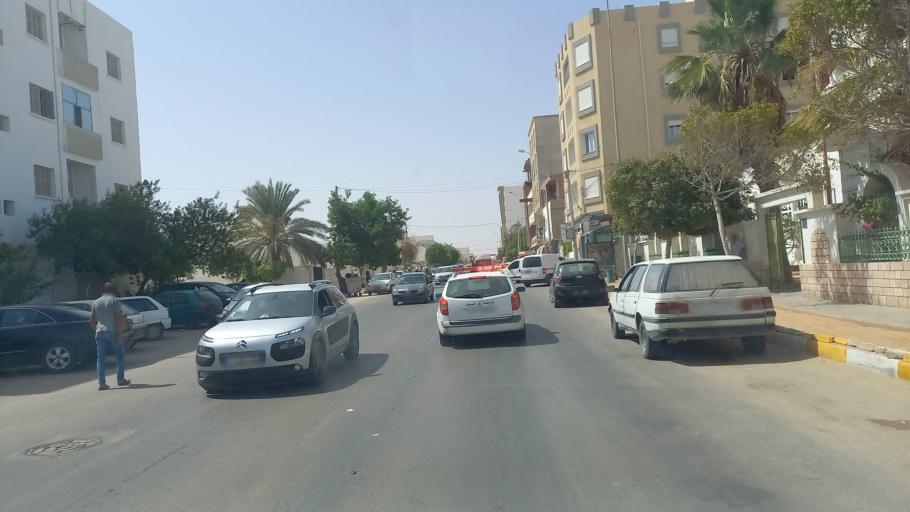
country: TN
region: Madanin
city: Medenine
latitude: 33.3407
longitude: 10.4879
